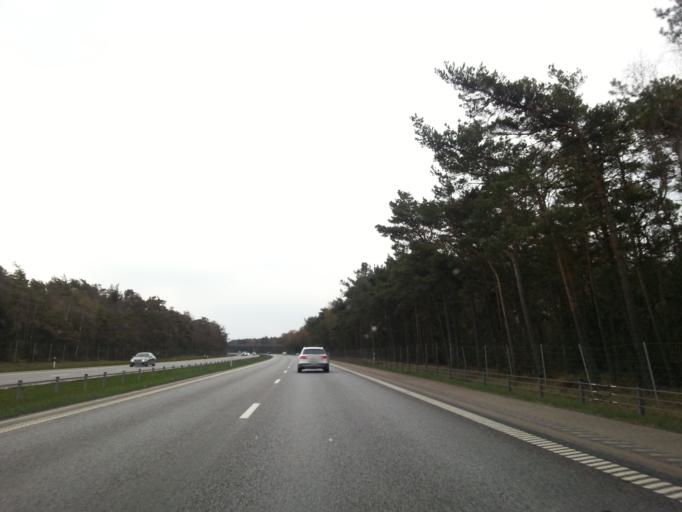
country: SE
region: Halland
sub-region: Halmstads Kommun
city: Paarp
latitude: 56.5713
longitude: 12.9486
